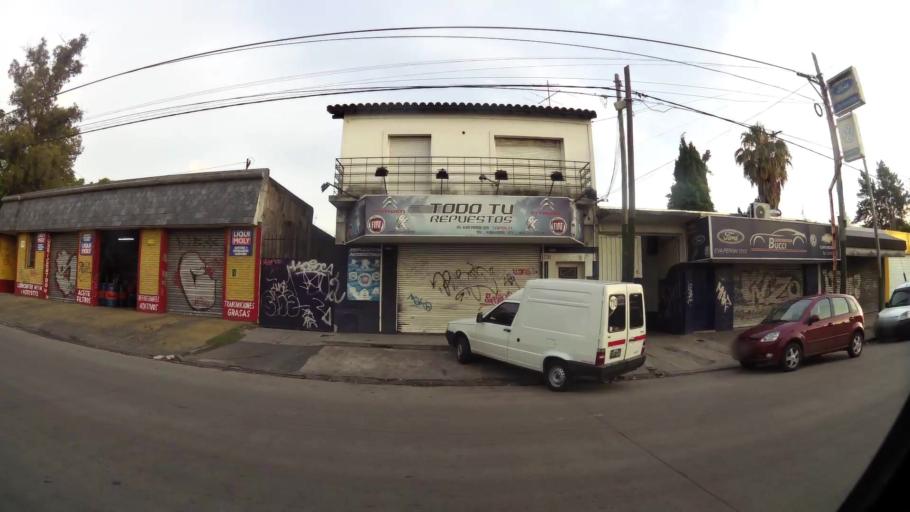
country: AR
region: Buenos Aires
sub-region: Partido de Lomas de Zamora
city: Lomas de Zamora
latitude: -34.7715
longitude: -58.3812
